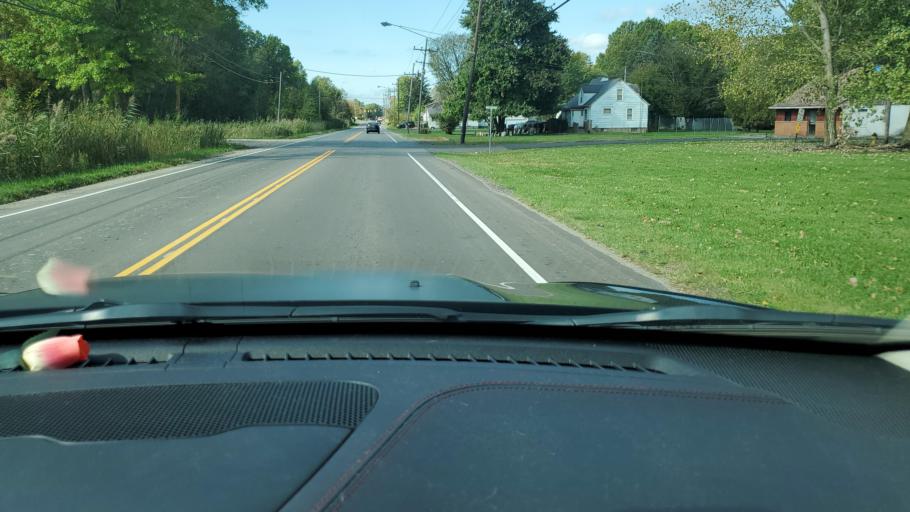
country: US
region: Ohio
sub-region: Trumbull County
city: Morgandale
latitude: 41.2655
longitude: -80.8082
